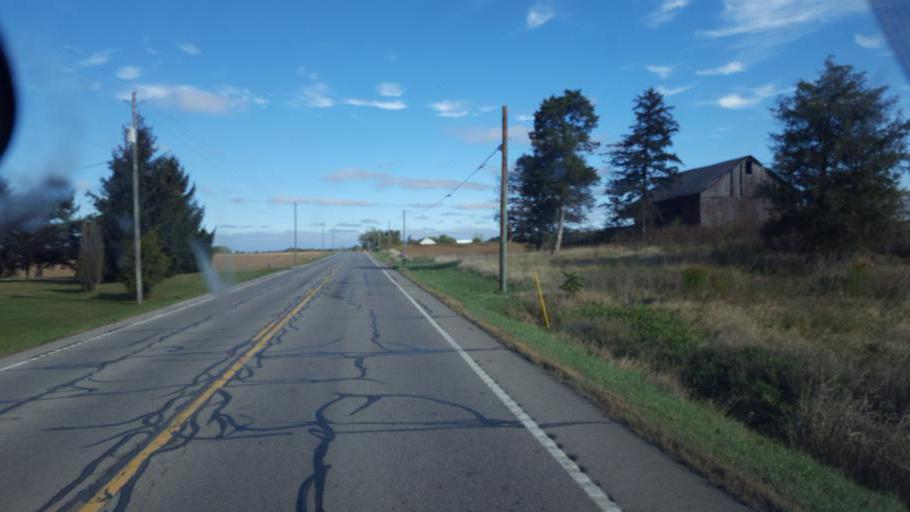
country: US
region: Ohio
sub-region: Huron County
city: Greenwich
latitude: 40.9627
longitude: -82.4953
